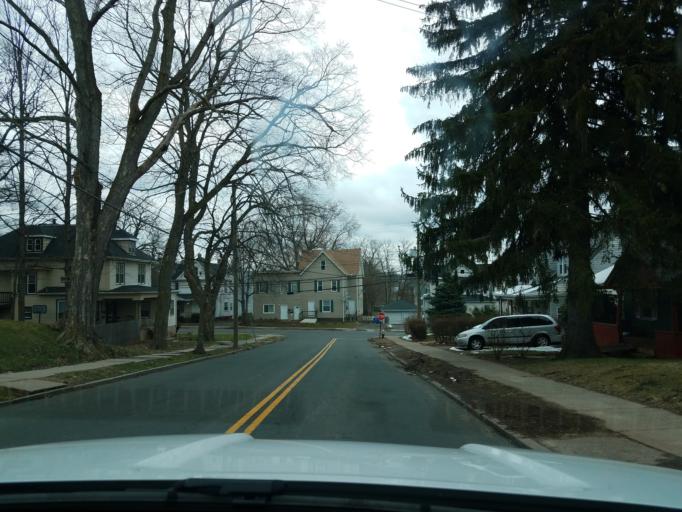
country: US
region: Connecticut
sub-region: Hartford County
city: New Britain
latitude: 41.6670
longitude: -72.7662
